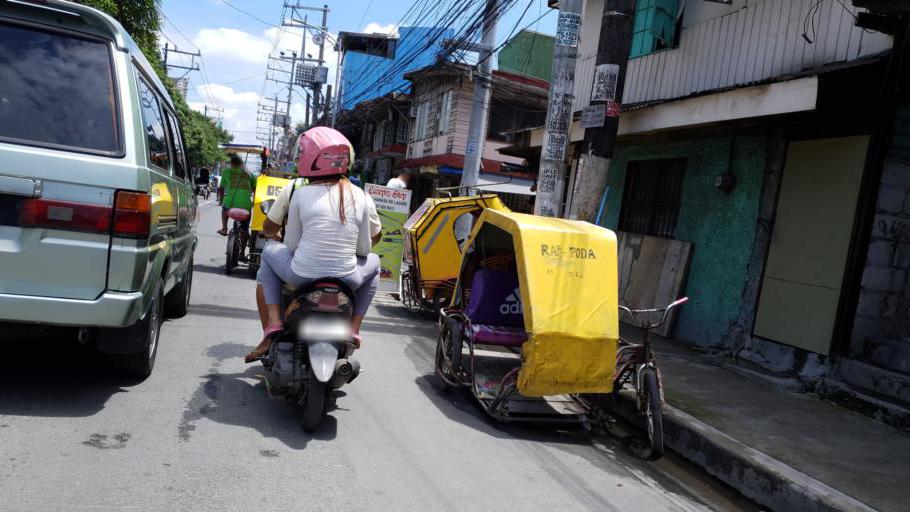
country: PH
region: Metro Manila
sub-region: City of Manila
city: Quiapo
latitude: 14.5754
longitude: 121.0053
